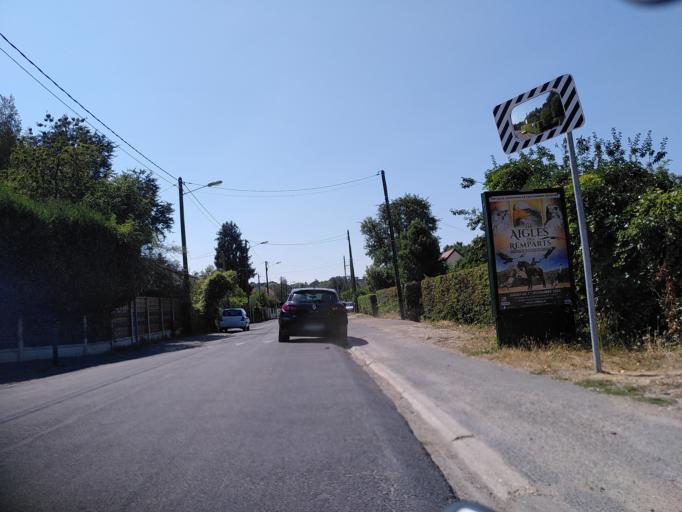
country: FR
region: Ile-de-France
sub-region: Departement de l'Essonne
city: Saint-Germain-les-Arpajon
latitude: 48.5983
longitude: 2.2652
